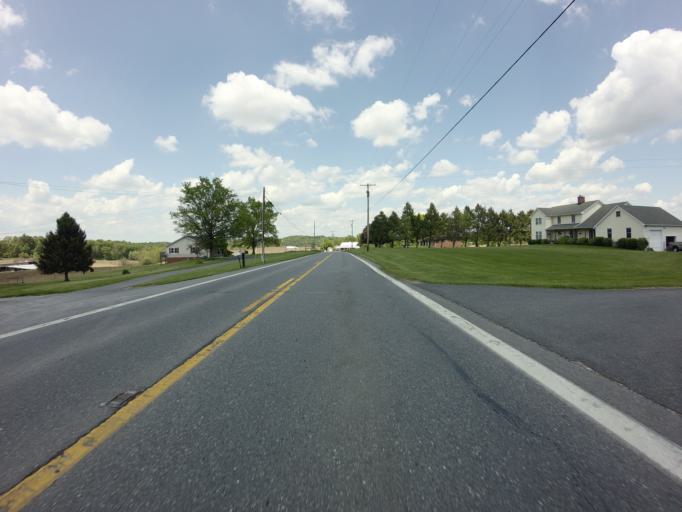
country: US
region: Maryland
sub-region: Frederick County
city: Green Valley
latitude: 39.2993
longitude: -77.3044
